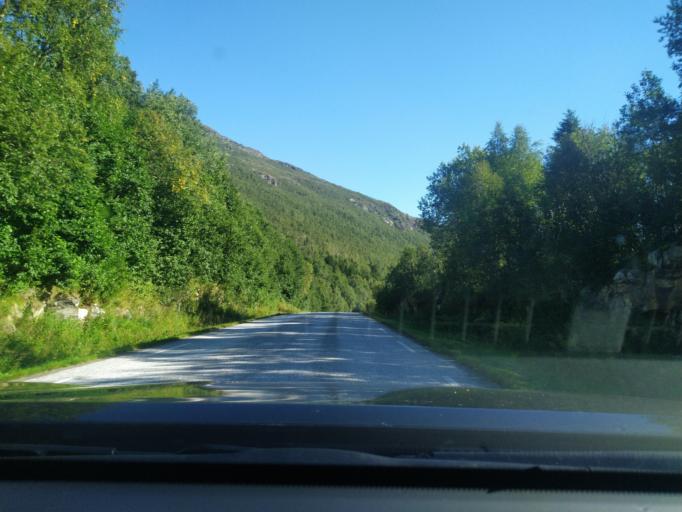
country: NO
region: Troms
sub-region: Dyroy
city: Brostadbotn
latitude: 68.9276
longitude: 17.6436
